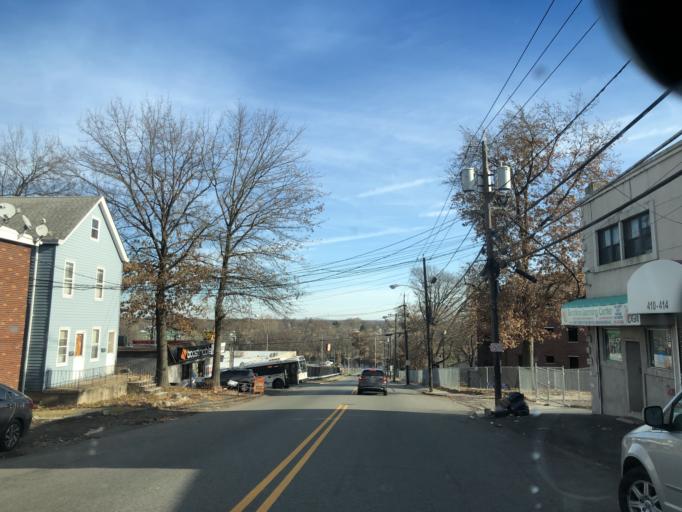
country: US
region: New Jersey
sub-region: Bergen County
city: Fair Lawn
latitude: 40.9331
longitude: -74.1443
